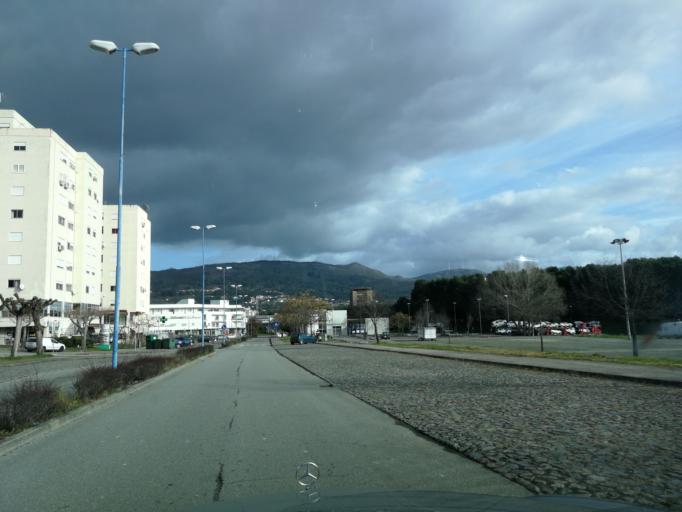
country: PT
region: Viana do Castelo
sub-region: Valenca
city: Valenca
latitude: 42.0227
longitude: -8.6449
